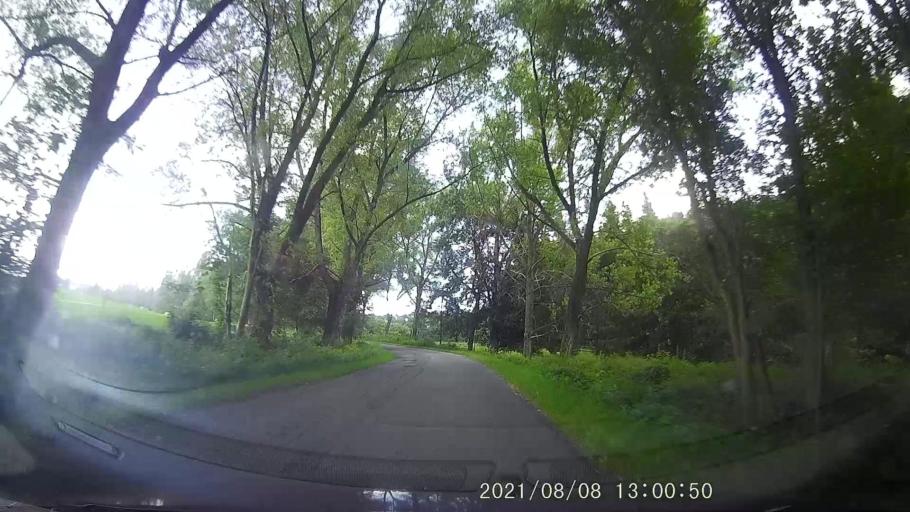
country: PL
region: Lower Silesian Voivodeship
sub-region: Powiat klodzki
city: Duszniki-Zdroj
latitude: 50.4163
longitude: 16.3419
